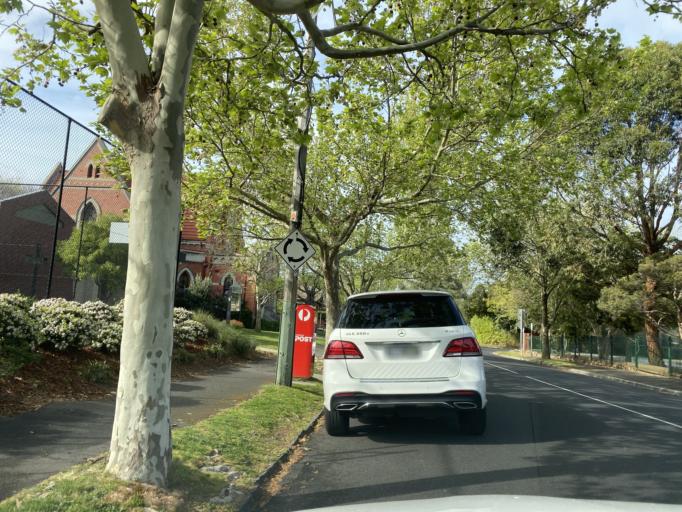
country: AU
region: Victoria
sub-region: Boroondara
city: Canterbury
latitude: -37.8311
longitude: 145.0857
